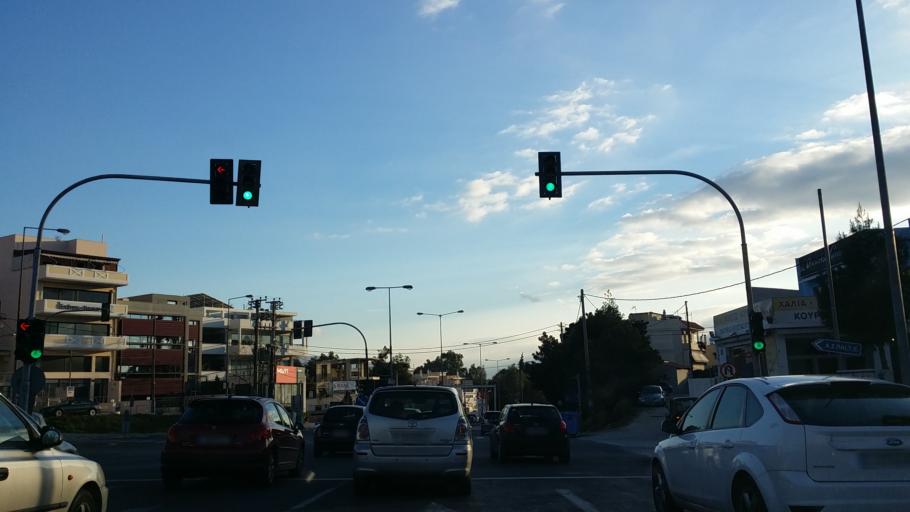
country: GR
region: Attica
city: Pefki
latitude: 38.0482
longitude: 23.7828
